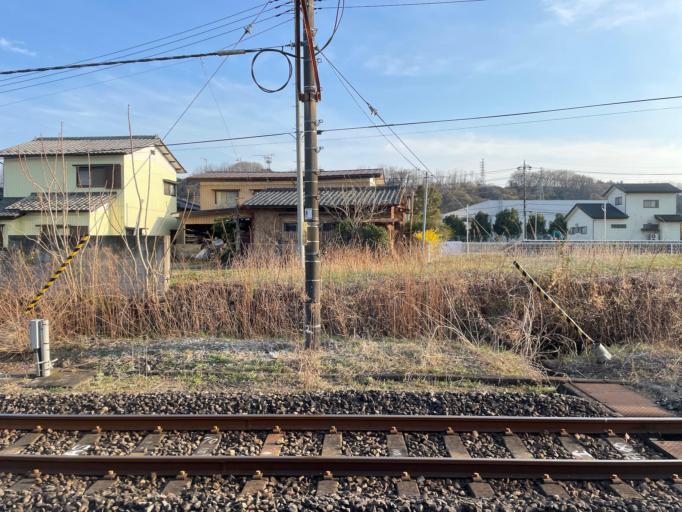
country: JP
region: Gunma
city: Annaka
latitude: 36.2984
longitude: 138.8485
